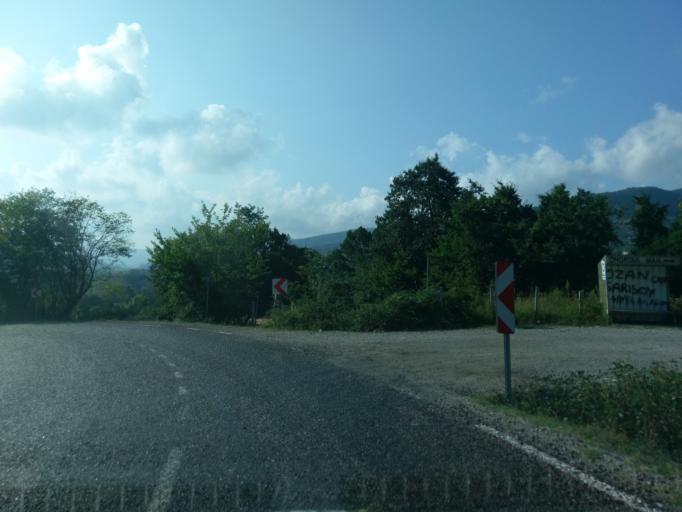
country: TR
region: Sinop
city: Ayancik
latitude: 41.8893
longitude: 34.4954
